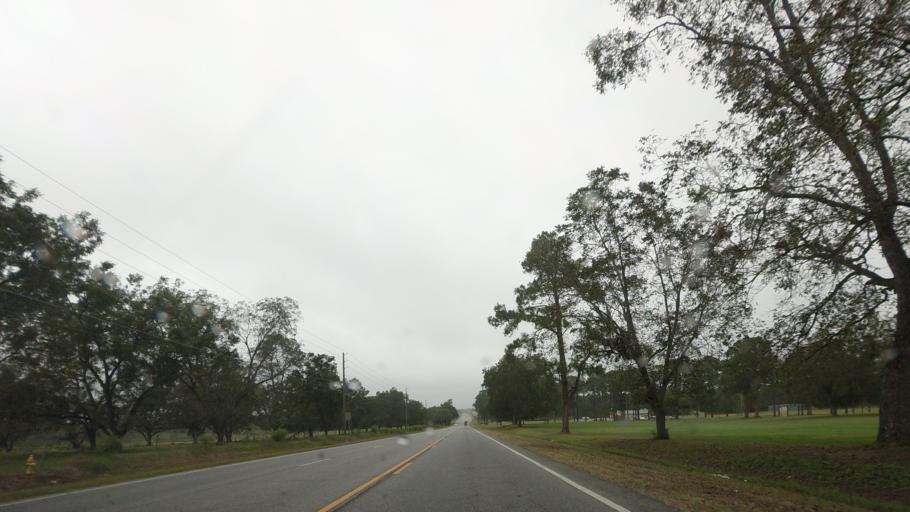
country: US
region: Georgia
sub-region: Ben Hill County
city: Fitzgerald
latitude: 31.6862
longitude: -83.2403
